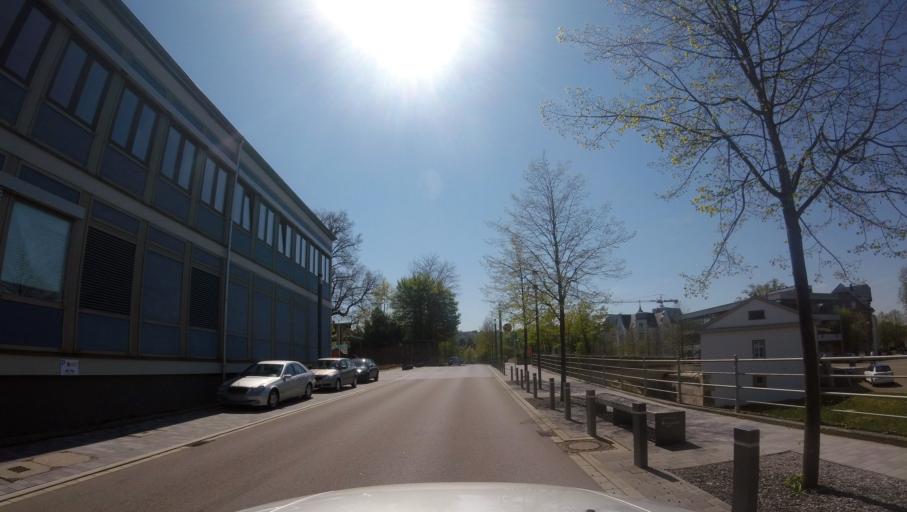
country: DE
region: Baden-Wuerttemberg
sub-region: Regierungsbezirk Stuttgart
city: Schwabisch Gmund
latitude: 48.8000
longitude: 9.7920
